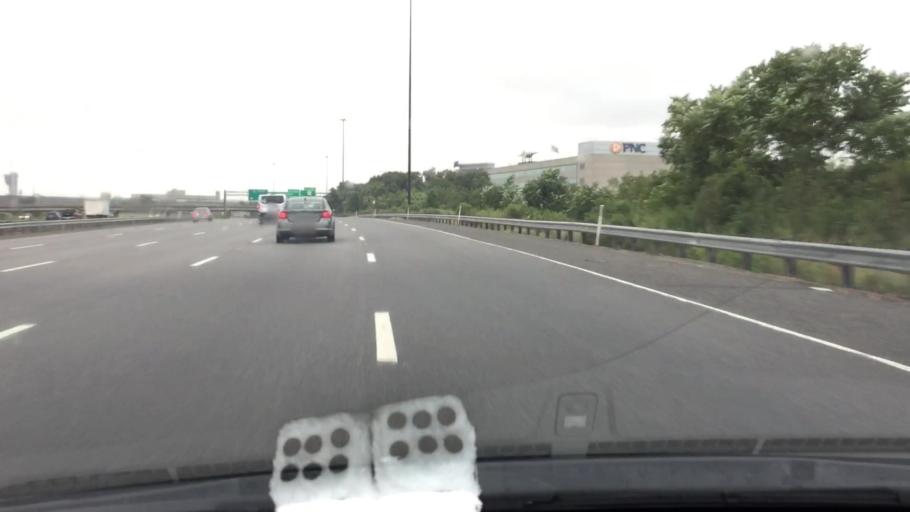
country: US
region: Pennsylvania
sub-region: Delaware County
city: Colwyn
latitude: 39.8889
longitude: -75.2435
